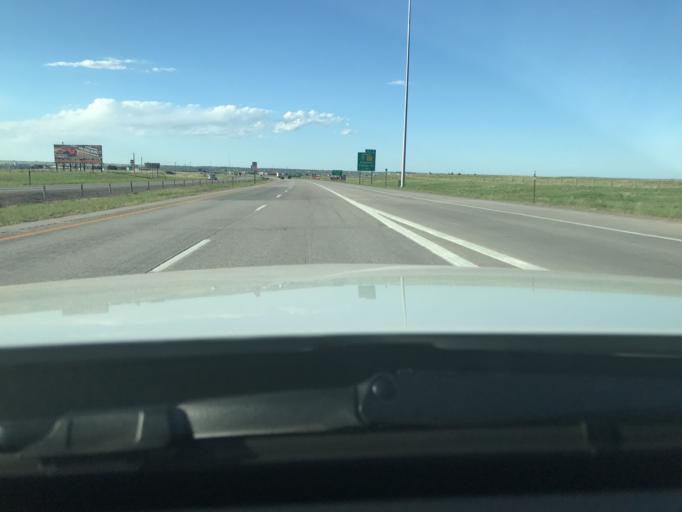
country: US
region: Wyoming
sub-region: Laramie County
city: South Greeley
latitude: 41.0862
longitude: -104.8520
